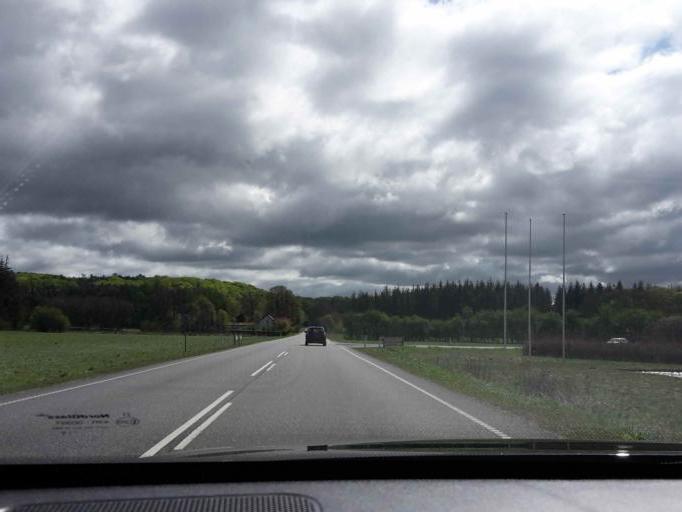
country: DK
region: Central Jutland
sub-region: Norddjurs Kommune
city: Auning
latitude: 56.4275
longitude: 10.3944
